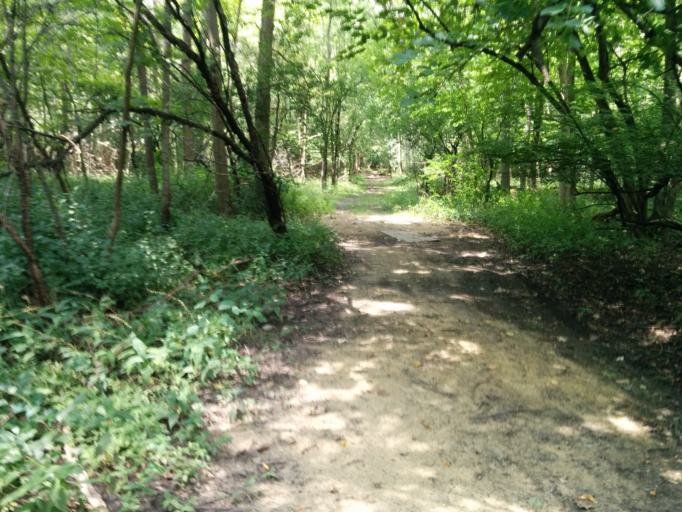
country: US
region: Illinois
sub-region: Lake County
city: Riverwoods
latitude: 42.1504
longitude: -87.9014
